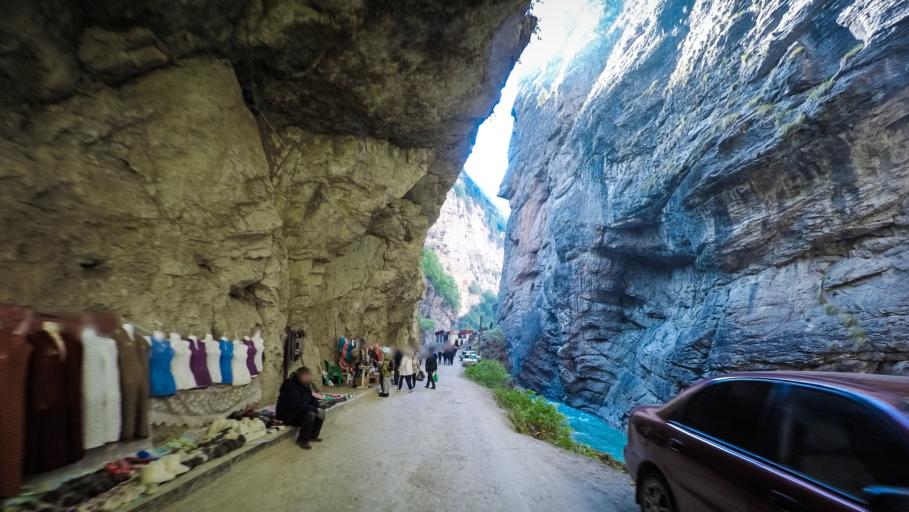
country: RU
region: Kabardino-Balkariya
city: Zhankhoteko
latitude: 43.4157
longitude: 43.2157
